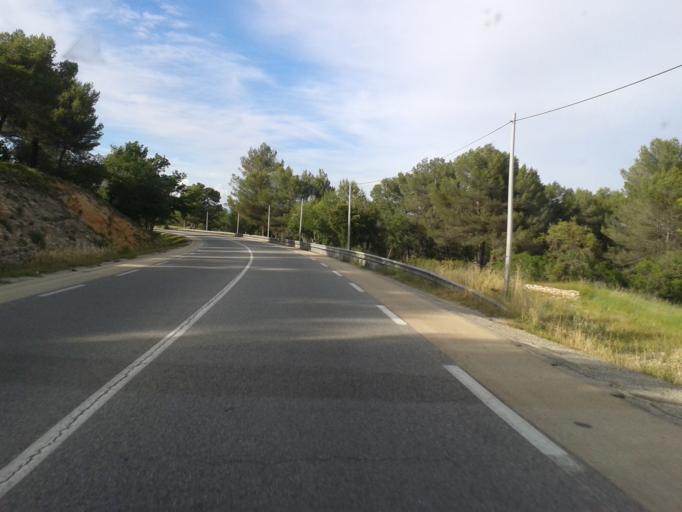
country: FR
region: Provence-Alpes-Cote d'Azur
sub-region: Departement des Bouches-du-Rhone
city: Meyrargues
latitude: 43.6230
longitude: 5.5082
